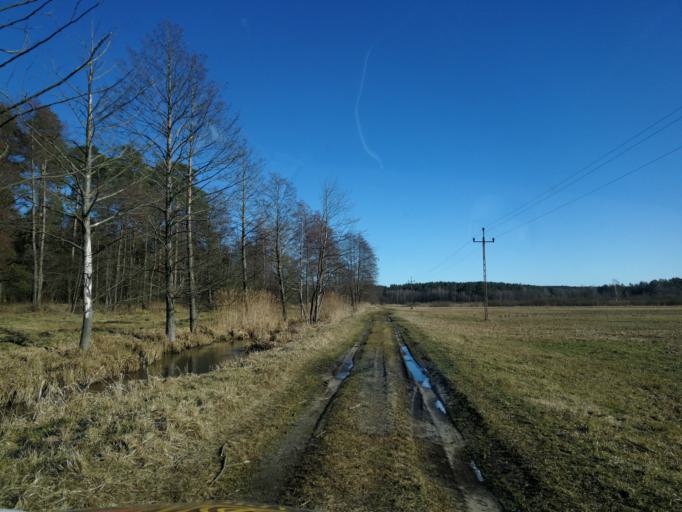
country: PL
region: Kujawsko-Pomorskie
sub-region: Powiat brodnicki
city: Gorzno
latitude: 53.2350
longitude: 19.6668
